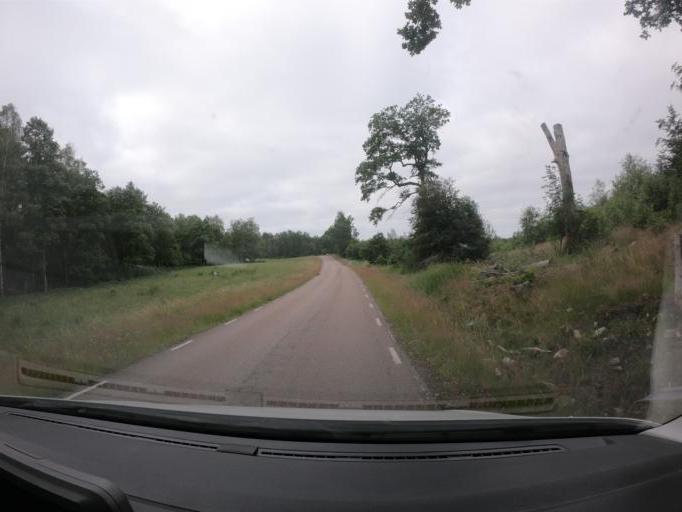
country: SE
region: Skane
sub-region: Perstorps Kommun
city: Perstorp
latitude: 56.0988
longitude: 13.3384
